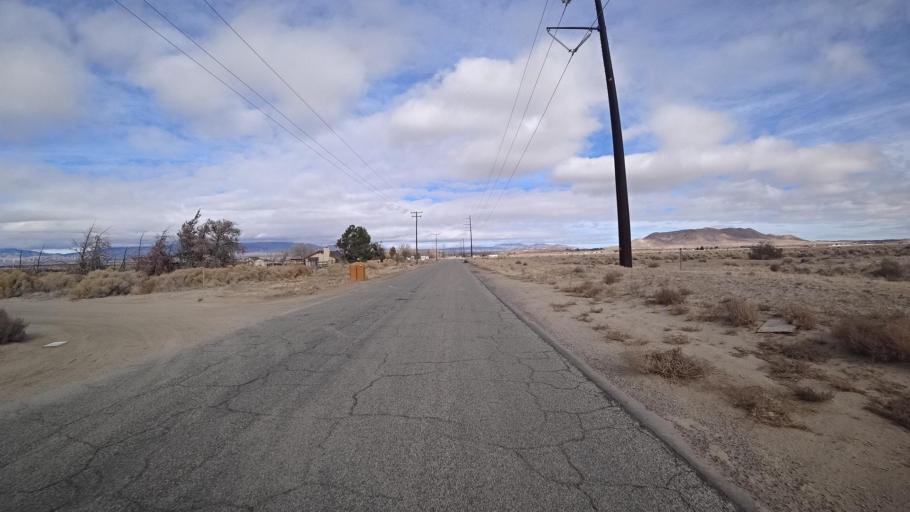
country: US
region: California
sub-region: Kern County
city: Rosamond
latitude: 34.8488
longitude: -118.3089
